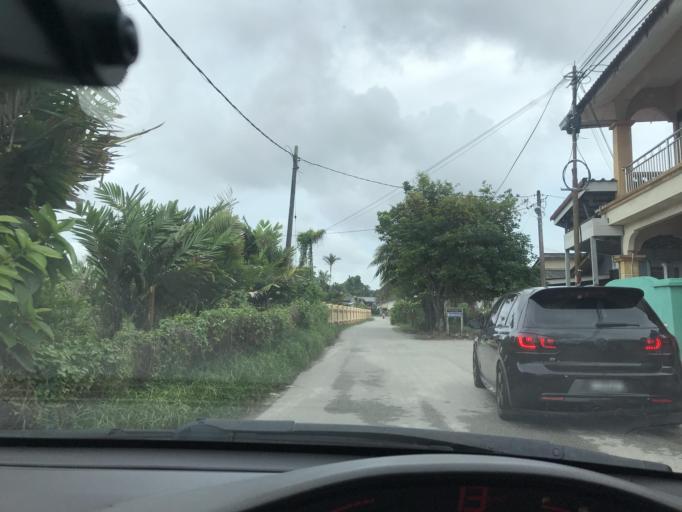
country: MY
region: Kelantan
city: Kota Bharu
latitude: 6.1138
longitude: 102.2174
